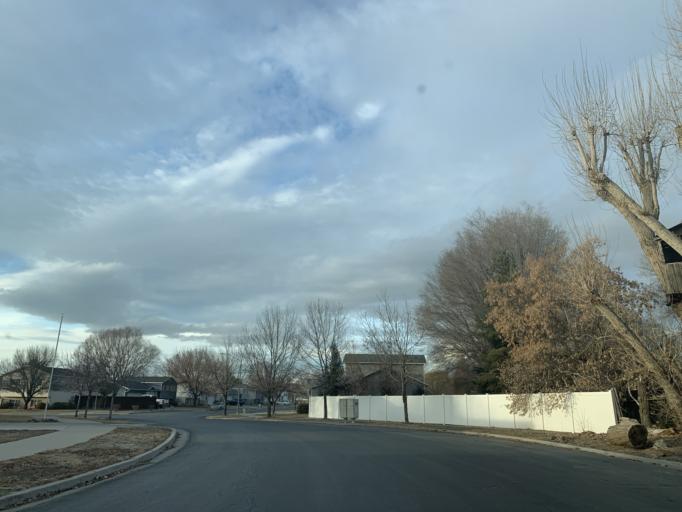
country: US
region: Utah
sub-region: Utah County
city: Provo
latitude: 40.2261
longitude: -111.6823
